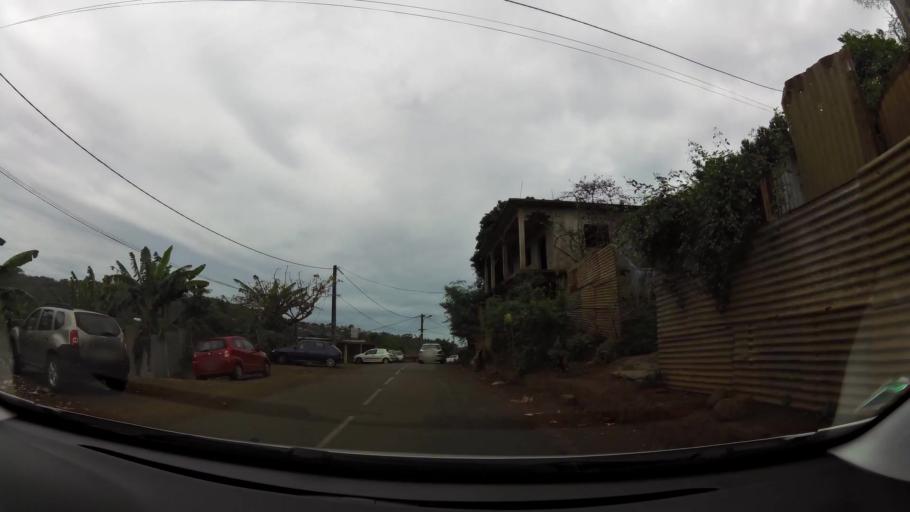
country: YT
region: Chiconi
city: Chiconi
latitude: -12.8376
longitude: 45.1178
